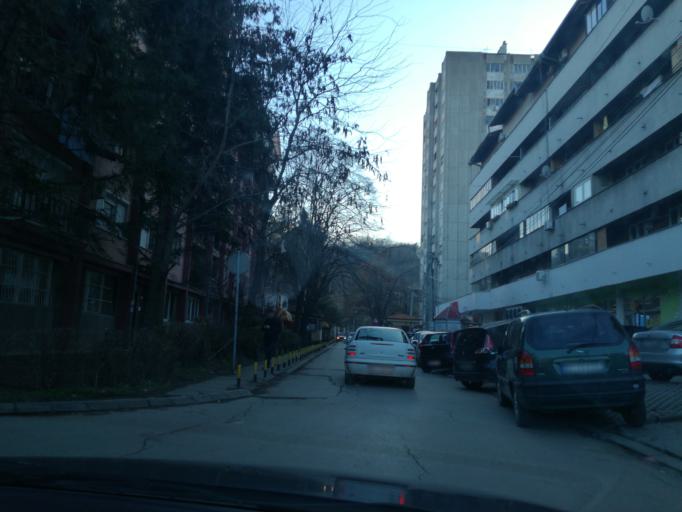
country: RS
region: Central Serbia
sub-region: Nisavski Okrug
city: Nis
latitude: 43.3122
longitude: 21.8883
